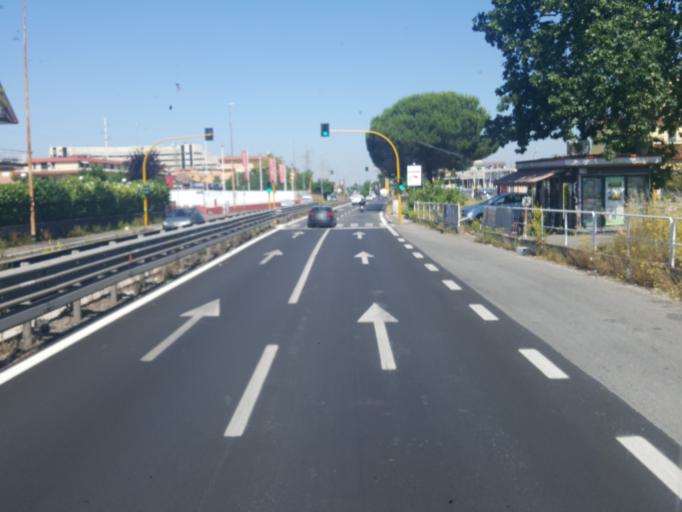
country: IT
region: Latium
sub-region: Citta metropolitana di Roma Capitale
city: Ciampino
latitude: 41.8362
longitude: 12.6018
